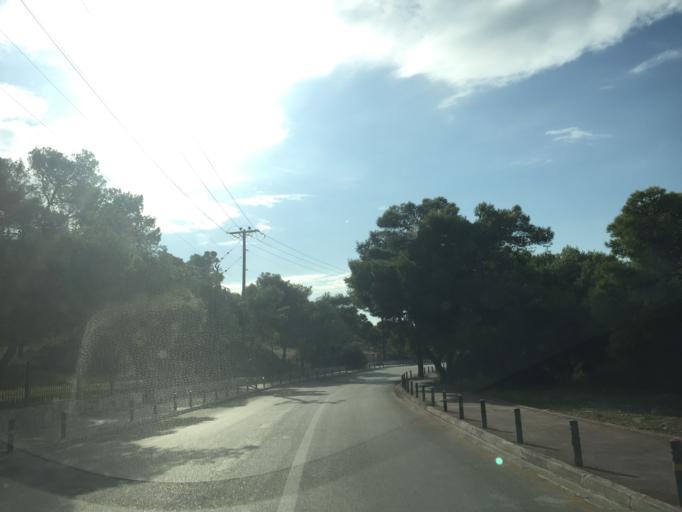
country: GR
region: Attica
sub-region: Nomarchia Anatolikis Attikis
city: Vouliagmeni
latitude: 37.8223
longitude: 23.7701
